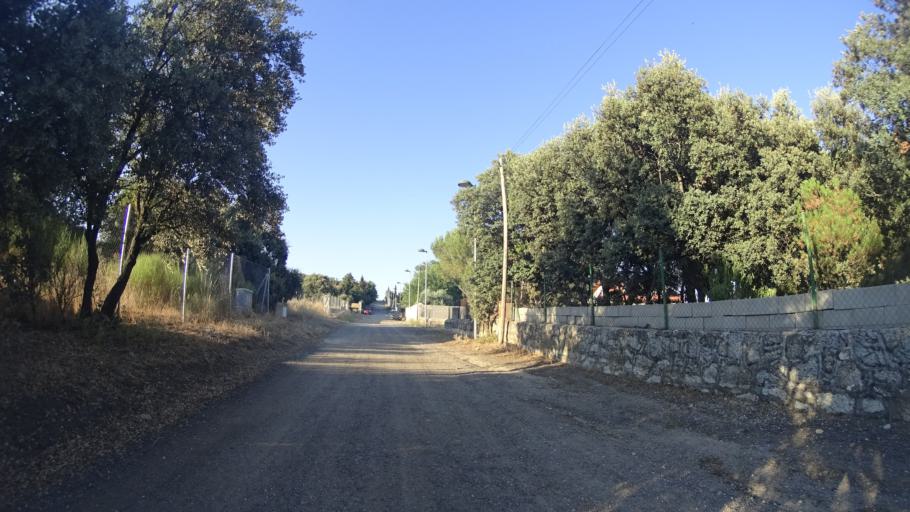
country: ES
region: Madrid
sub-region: Provincia de Madrid
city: Galapagar
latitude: 40.5640
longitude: -4.0015
